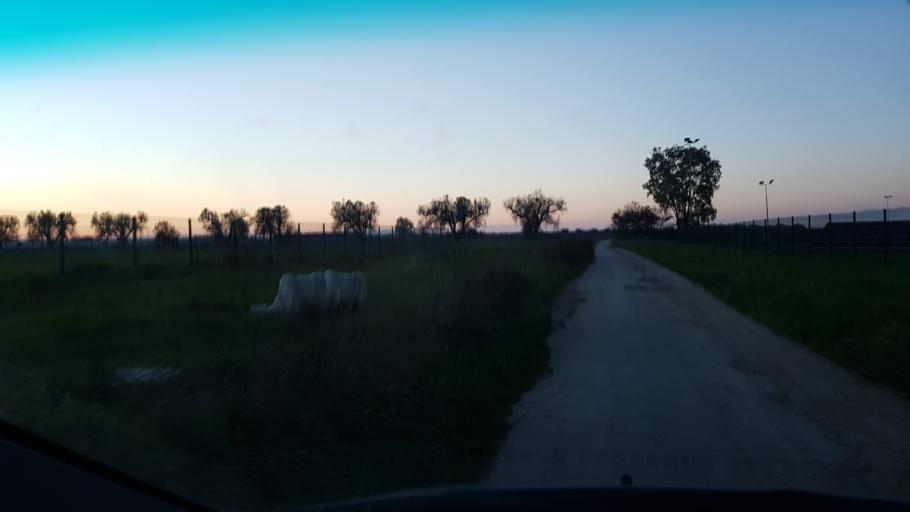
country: IT
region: Apulia
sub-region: Provincia di Brindisi
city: San Pietro Vernotico
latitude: 40.5074
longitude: 17.9728
